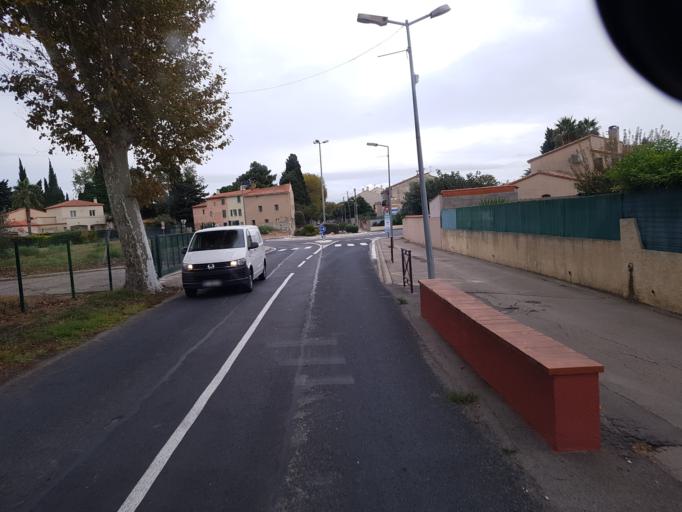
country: FR
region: Languedoc-Roussillon
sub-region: Departement des Pyrenees-Orientales
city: Torreilles
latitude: 42.7599
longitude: 2.9900
